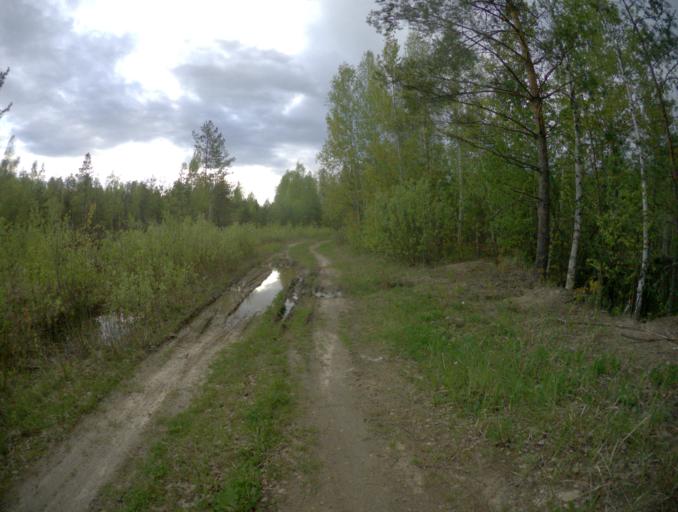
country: RU
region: Vladimir
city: Anopino
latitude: 55.7160
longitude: 40.6043
